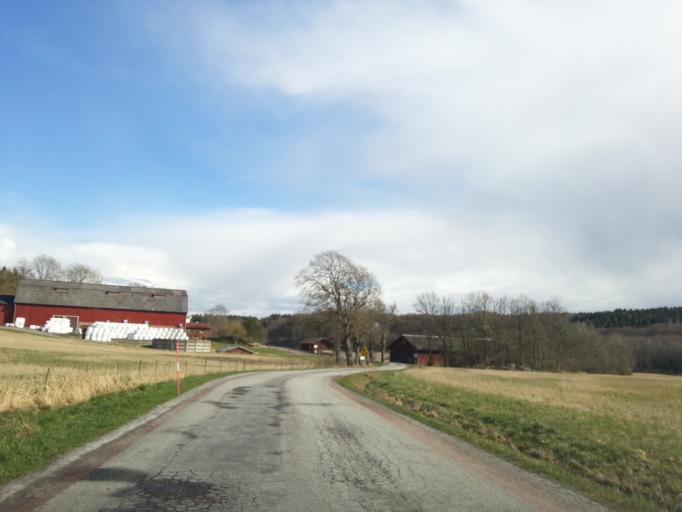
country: SE
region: Vaestra Goetaland
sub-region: Kungalvs Kommun
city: Kungalv
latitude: 57.8838
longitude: 12.0026
